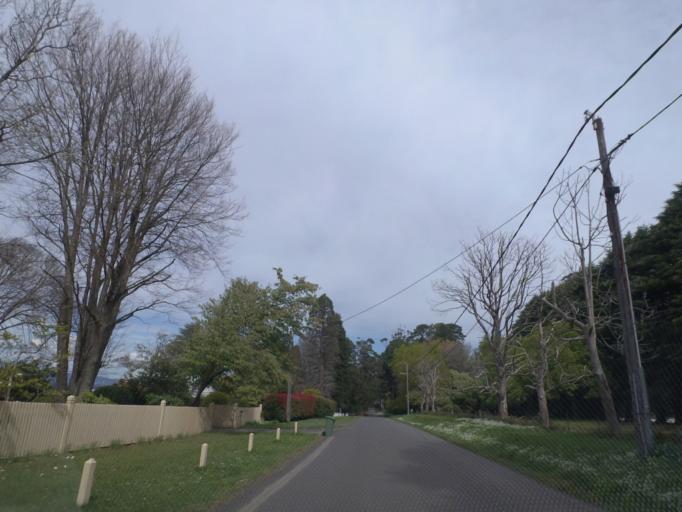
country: AU
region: Victoria
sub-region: Yarra Ranges
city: Mount Dandenong
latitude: -37.8263
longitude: 145.3641
